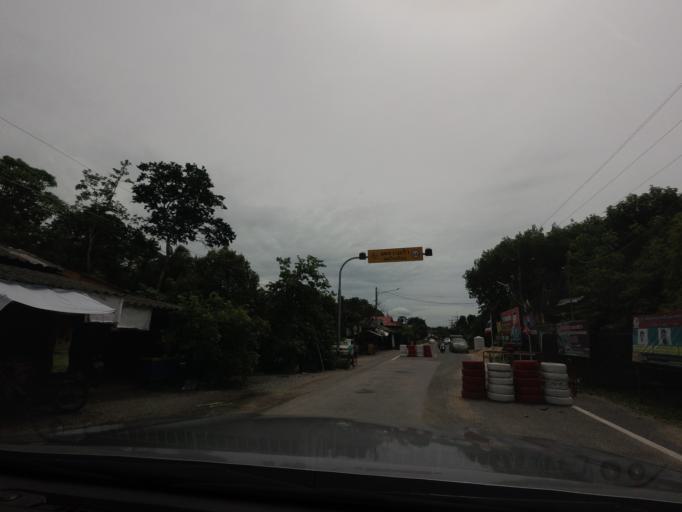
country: TH
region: Pattani
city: Kapho
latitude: 6.6344
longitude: 101.5489
